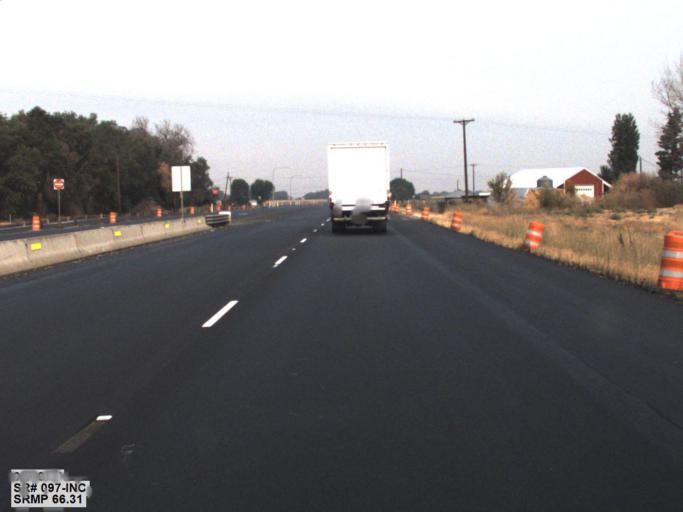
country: US
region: Washington
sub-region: Yakima County
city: Wapato
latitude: 46.4168
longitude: -120.3958
